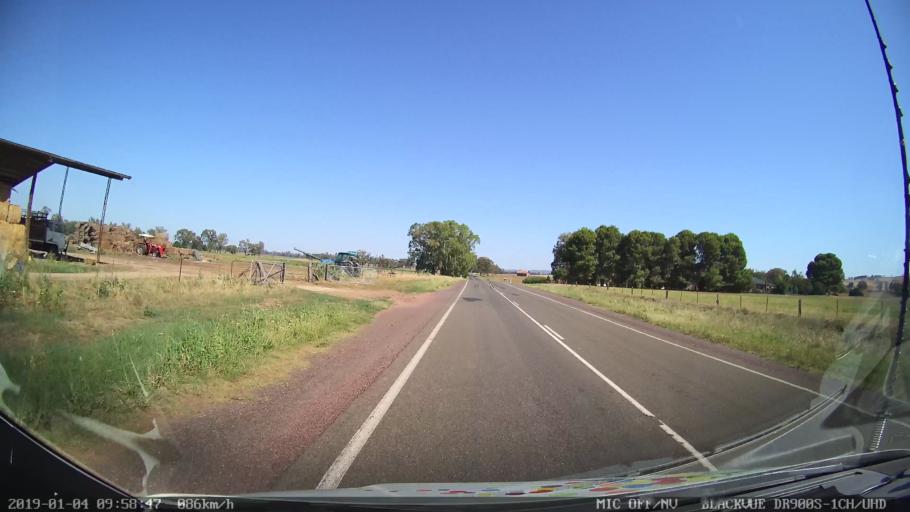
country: AU
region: New South Wales
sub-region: Cabonne
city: Canowindra
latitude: -33.5147
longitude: 148.3915
